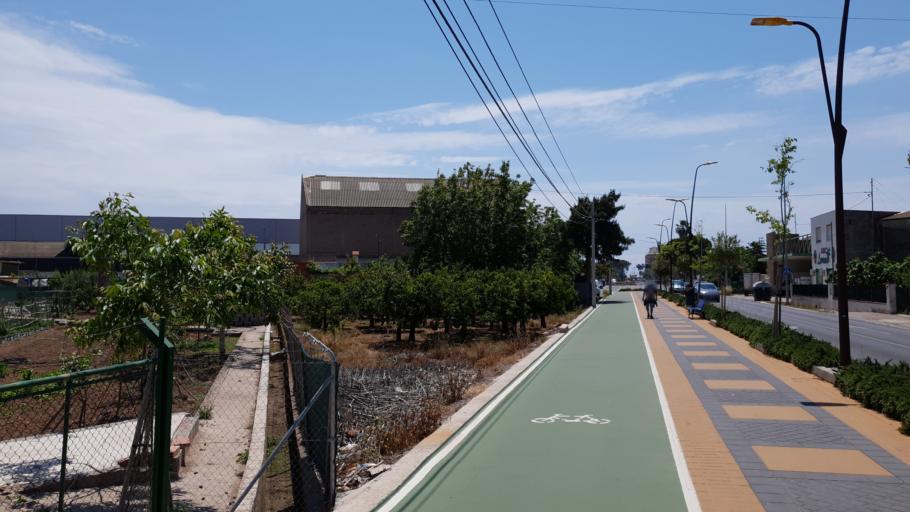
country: ES
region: Valencia
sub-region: Provincia de Castello
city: Burriana
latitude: 39.8724
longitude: -0.0751
